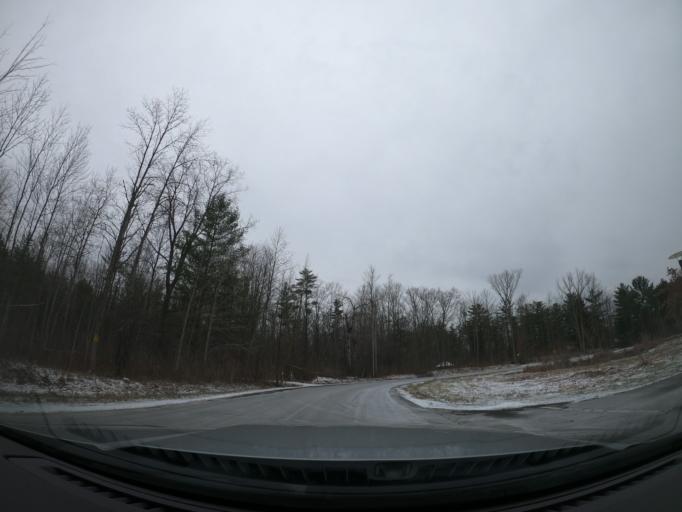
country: US
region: New York
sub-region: Tompkins County
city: Northeast Ithaca
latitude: 42.4800
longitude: -76.4490
